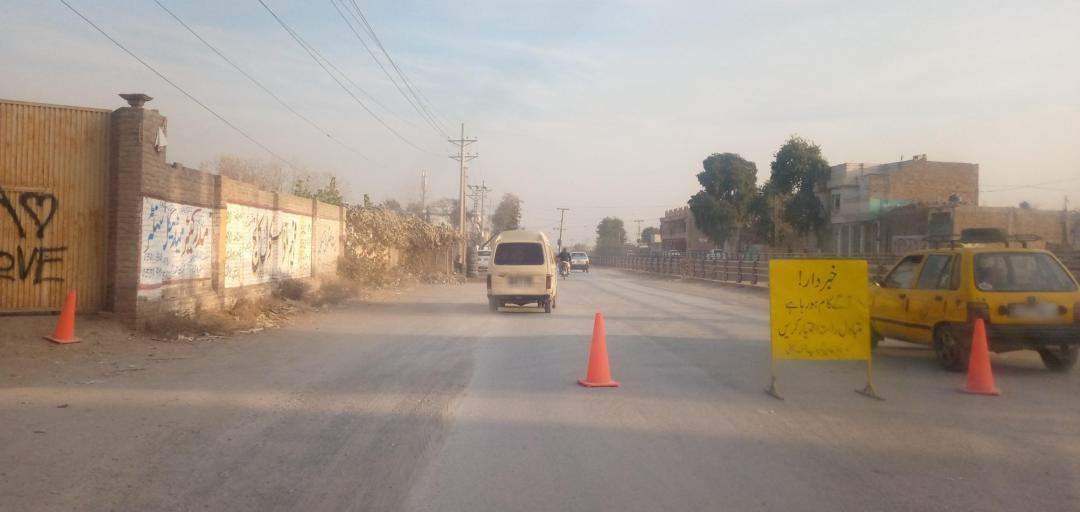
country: PK
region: Khyber Pakhtunkhwa
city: Peshawar
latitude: 33.9705
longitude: 71.5351
